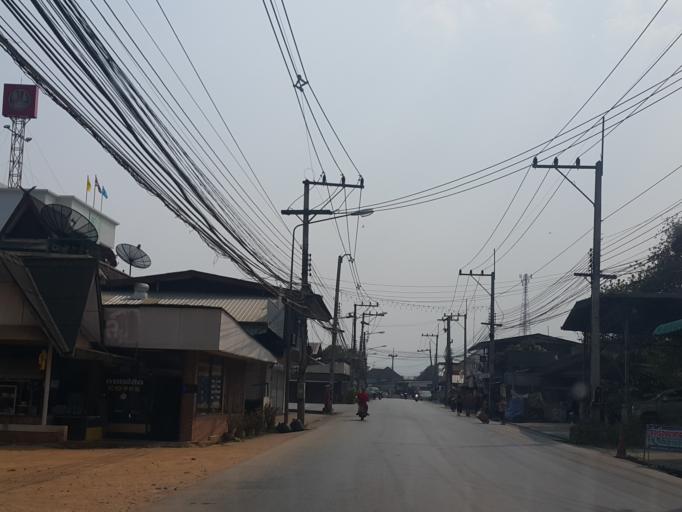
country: TH
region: Chiang Mai
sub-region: Amphoe Chiang Dao
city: Chiang Dao
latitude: 19.3729
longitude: 98.9659
